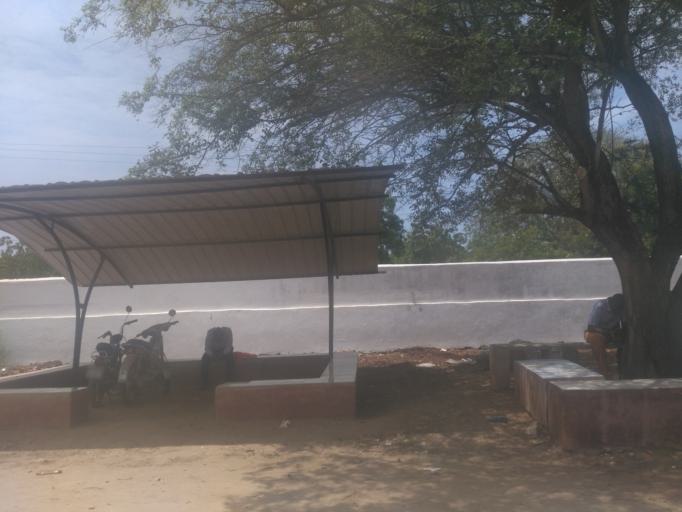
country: TZ
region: Zanzibar Urban/West
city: Zanzibar
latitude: -6.2174
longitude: 39.2126
